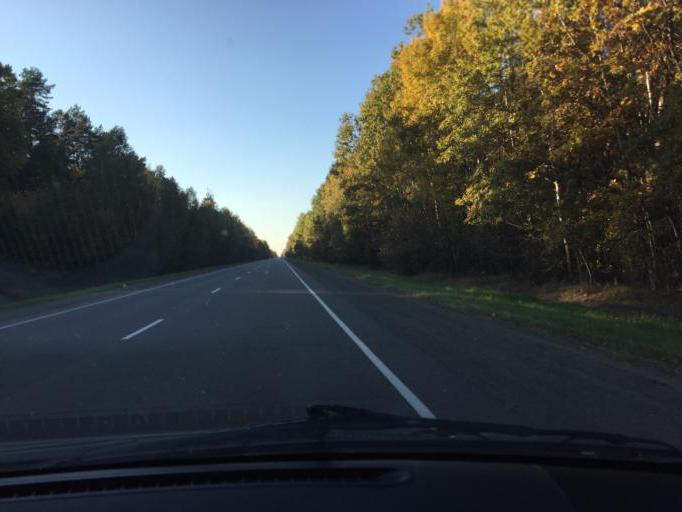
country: BY
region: Brest
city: Horad Luninyets
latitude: 52.2945
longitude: 26.7545
